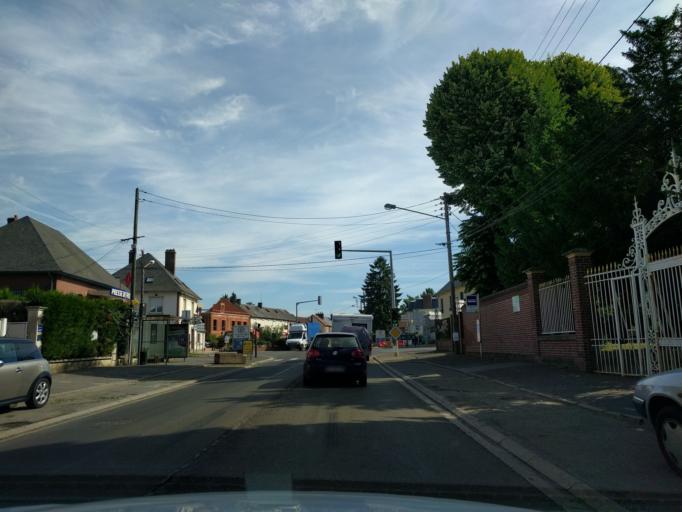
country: FR
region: Picardie
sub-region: Departement de l'Oise
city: Breteuil
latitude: 49.5669
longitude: 2.2218
